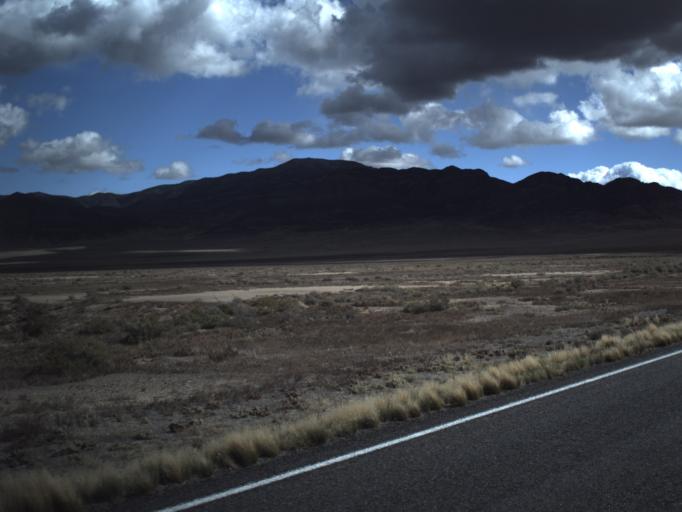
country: US
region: Utah
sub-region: Beaver County
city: Milford
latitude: 38.5254
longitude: -113.6631
